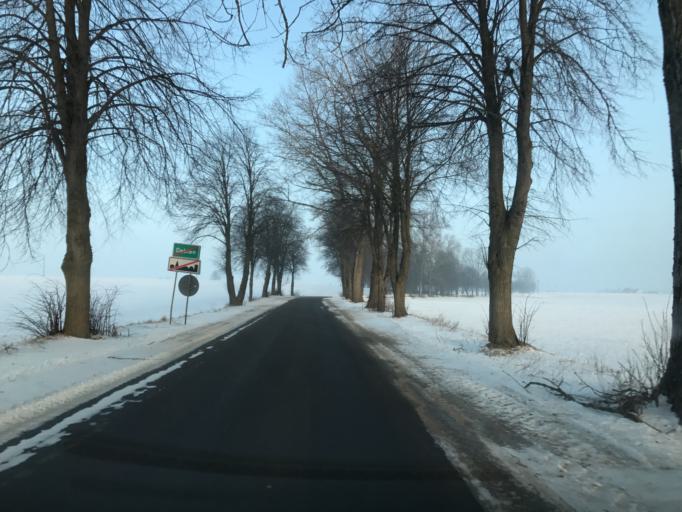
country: PL
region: Warmian-Masurian Voivodeship
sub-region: Powiat dzialdowski
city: Rybno
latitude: 53.3966
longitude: 19.8955
